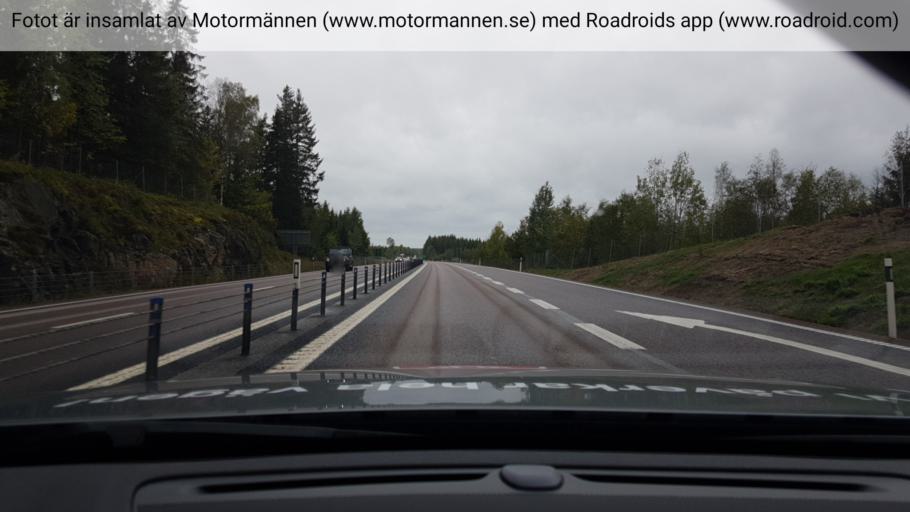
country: SE
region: Vaermland
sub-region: Karlstads Kommun
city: Skattkarr
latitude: 59.3911
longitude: 13.8473
